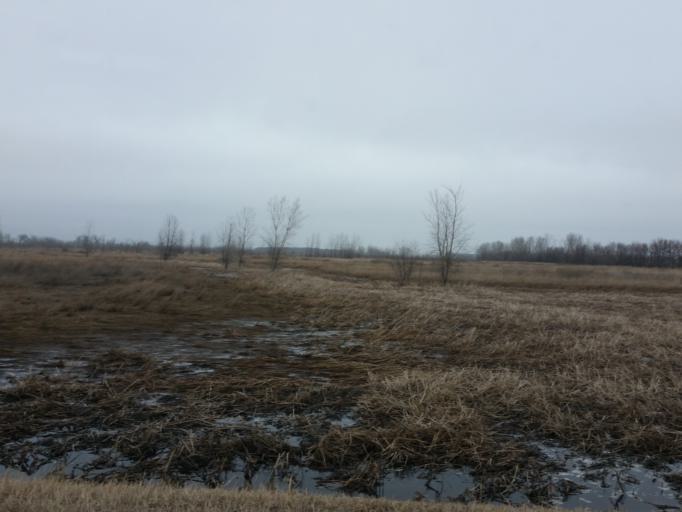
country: US
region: North Dakota
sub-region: Walsh County
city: Grafton
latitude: 48.3613
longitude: -97.1672
